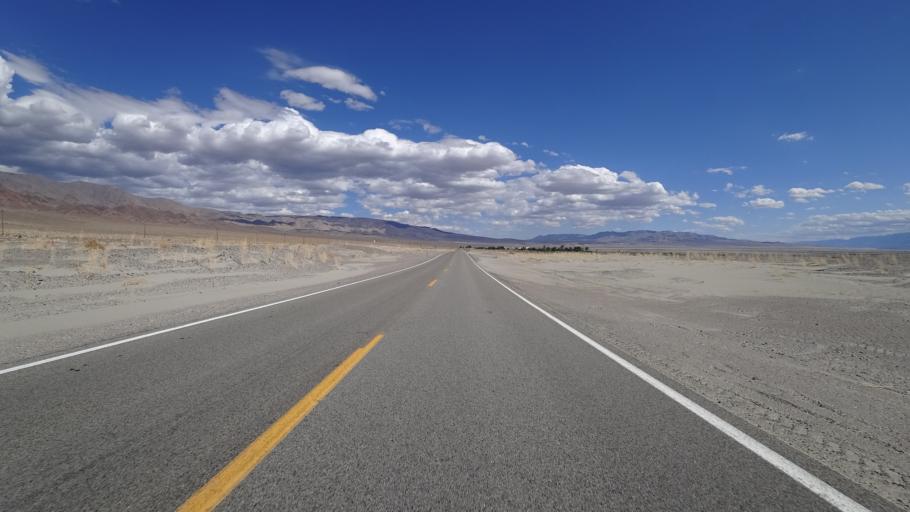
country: US
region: California
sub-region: Inyo County
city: Lone Pine
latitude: 36.4994
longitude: -117.8817
